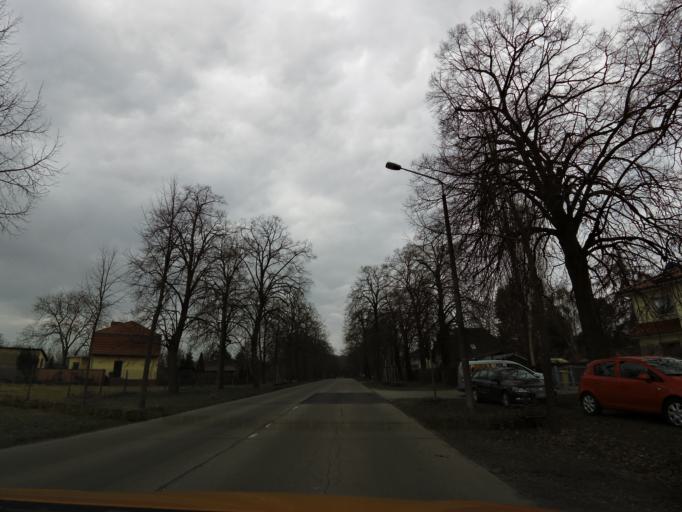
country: DE
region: Brandenburg
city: Potsdam
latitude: 52.4233
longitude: 13.0267
